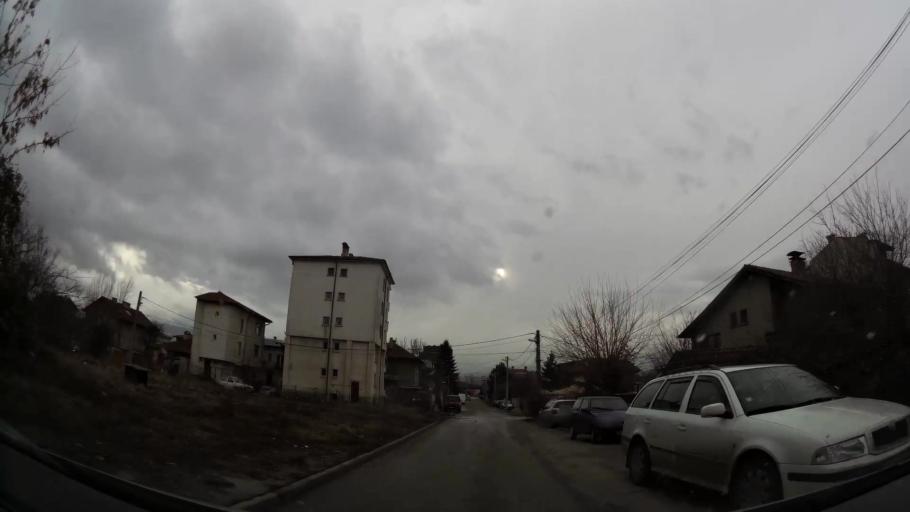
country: BG
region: Sofia-Capital
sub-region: Stolichna Obshtina
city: Sofia
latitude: 42.7257
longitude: 23.2692
